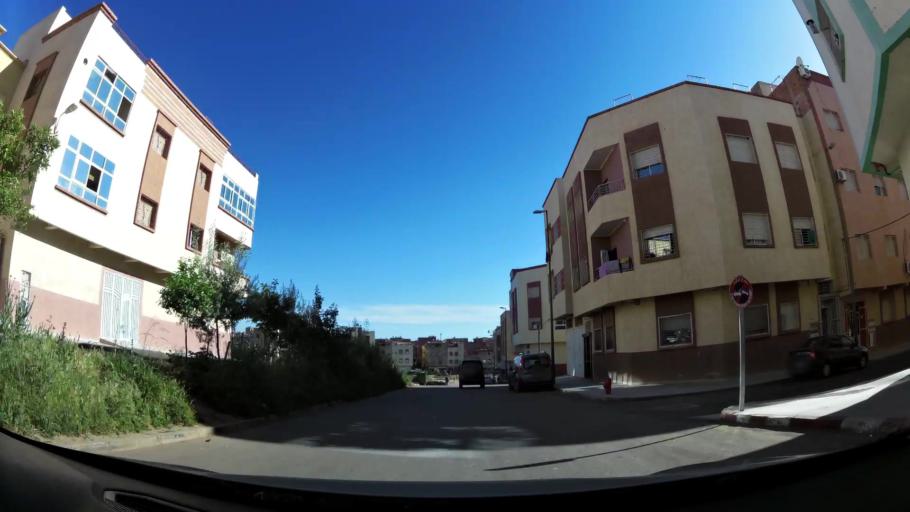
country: MA
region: Meknes-Tafilalet
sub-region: Meknes
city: Meknes
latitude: 33.8625
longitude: -5.5847
